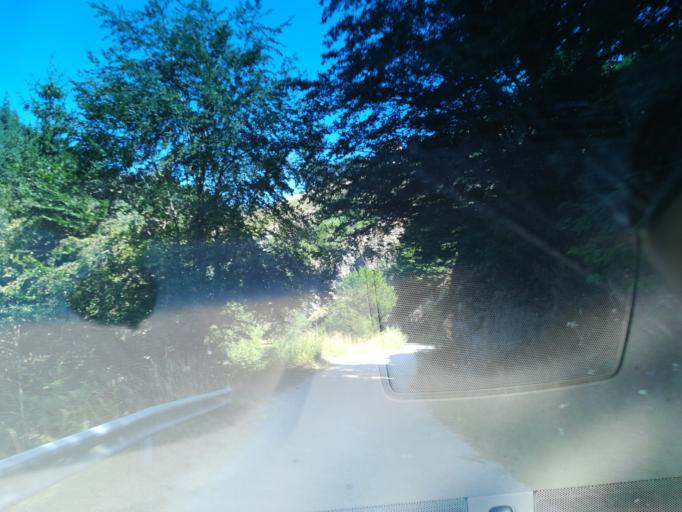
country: BG
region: Smolyan
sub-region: Obshtina Smolyan
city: Smolyan
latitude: 41.6583
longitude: 24.8278
